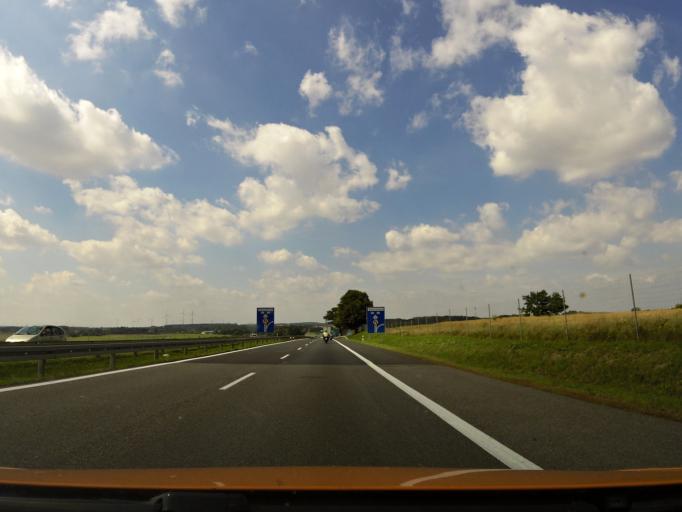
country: PL
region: West Pomeranian Voivodeship
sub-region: Powiat policki
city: Kolbaskowo
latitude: 53.3417
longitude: 14.4655
